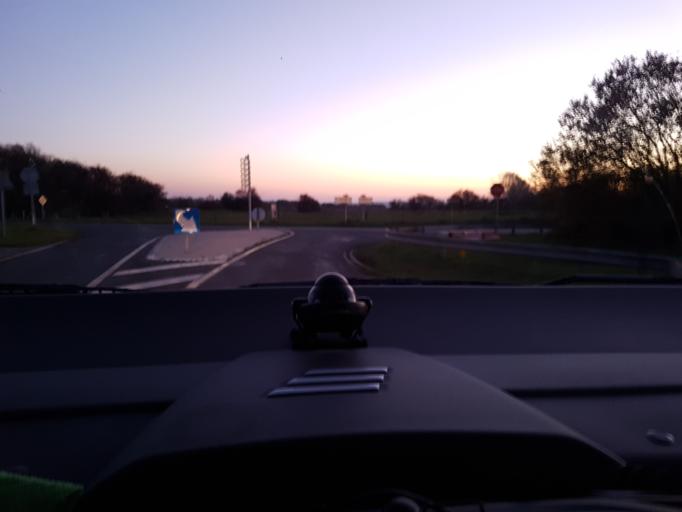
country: FR
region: Picardie
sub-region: Departement de la Somme
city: Saint-Valery-sur-Somme
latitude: 50.1978
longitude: 1.6931
